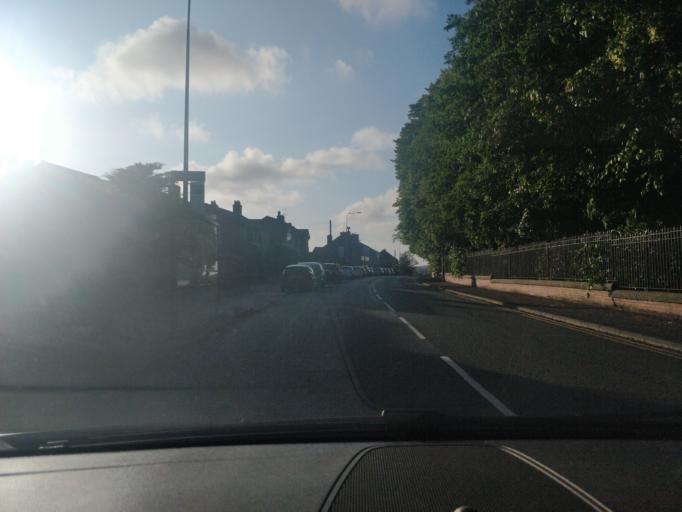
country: GB
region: England
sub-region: St. Helens
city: Billinge
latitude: 53.5182
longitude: -2.7127
